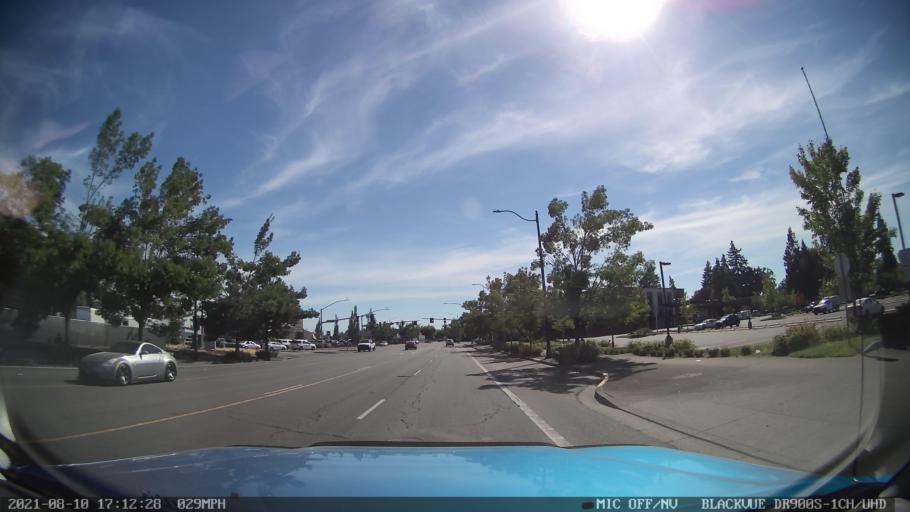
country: US
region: Oregon
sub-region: Marion County
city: Salem
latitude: 44.9611
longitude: -123.0149
